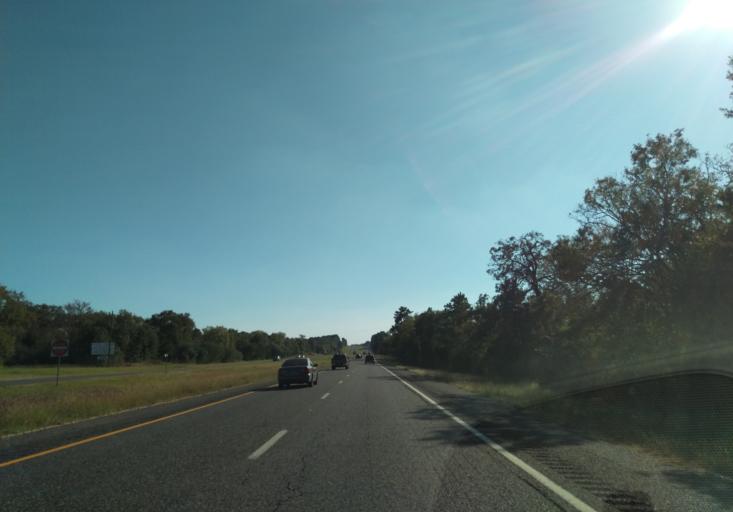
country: US
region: Texas
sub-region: Waller County
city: Hempstead
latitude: 30.2271
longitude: -96.0555
